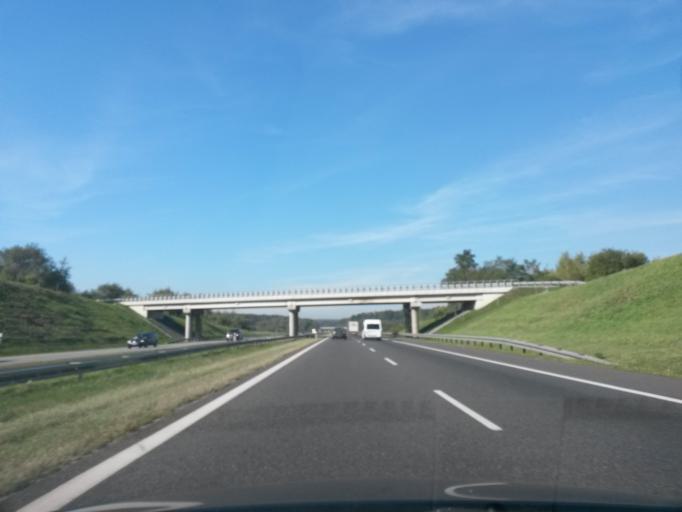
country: PL
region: Lesser Poland Voivodeship
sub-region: Powiat krakowski
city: Czulow
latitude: 50.0846
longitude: 19.6994
